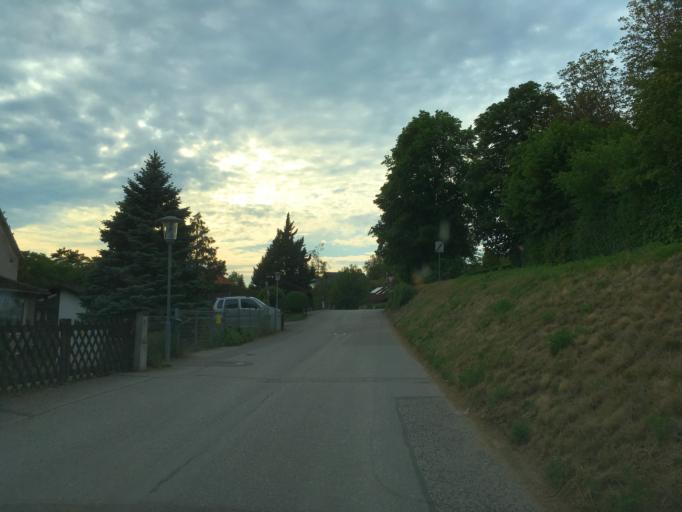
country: AT
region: Lower Austria
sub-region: Politischer Bezirk Sankt Polten
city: Maria-Anzbach
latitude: 48.1917
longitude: 15.9342
